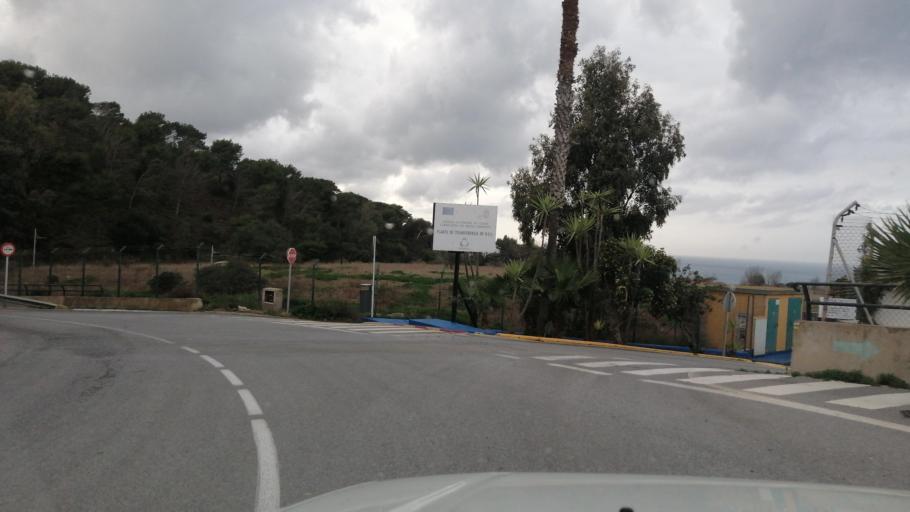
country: ES
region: Ceuta
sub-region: Ceuta
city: Ceuta
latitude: 35.9010
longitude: -5.2851
